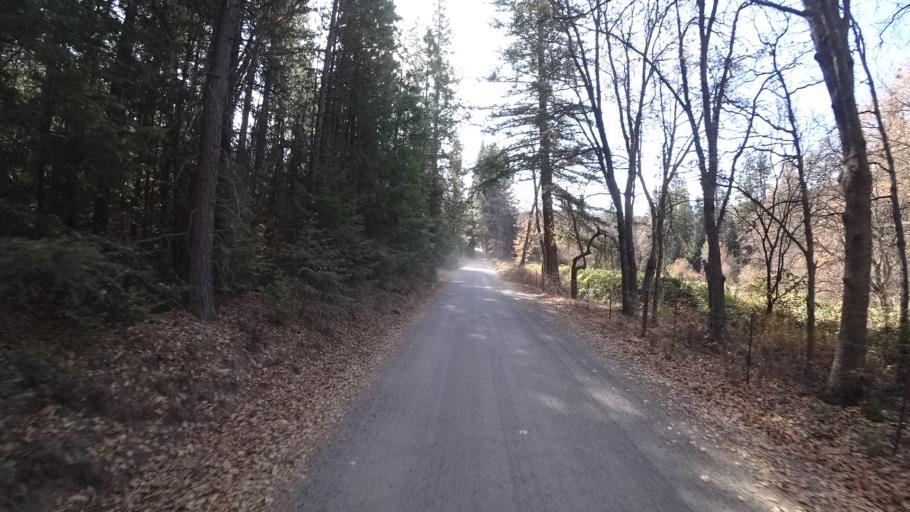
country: US
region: California
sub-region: Siskiyou County
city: Weed
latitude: 41.4428
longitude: -122.4241
